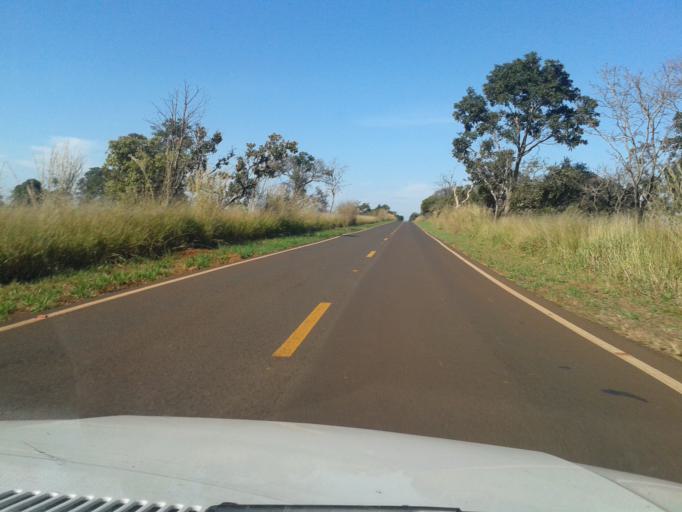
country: BR
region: Minas Gerais
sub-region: Ituiutaba
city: Ituiutaba
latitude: -19.0568
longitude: -49.7667
